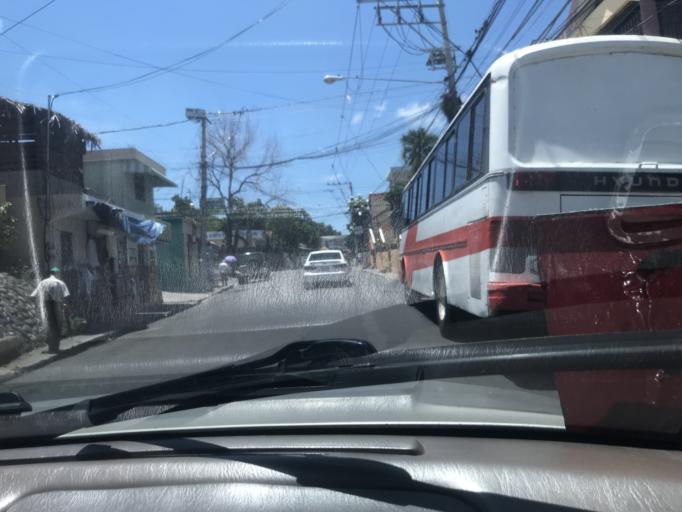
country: DO
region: Santiago
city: Santiago de los Caballeros
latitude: 19.4257
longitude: -70.6922
